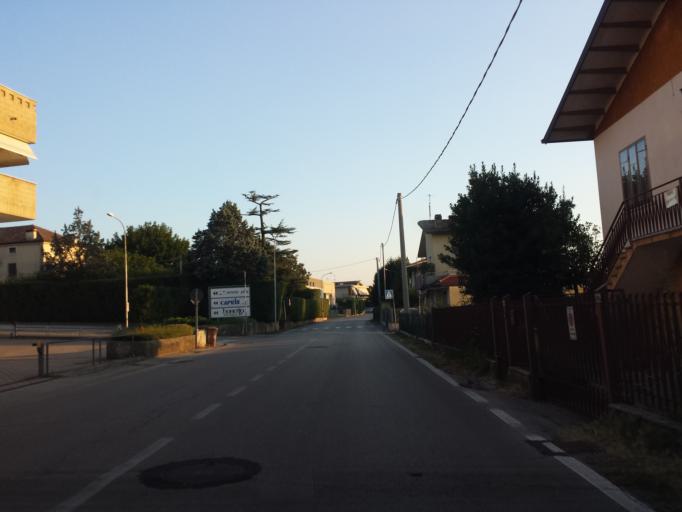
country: IT
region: Veneto
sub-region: Provincia di Vicenza
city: Monticello Conte Otto
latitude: 45.5855
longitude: 11.5664
